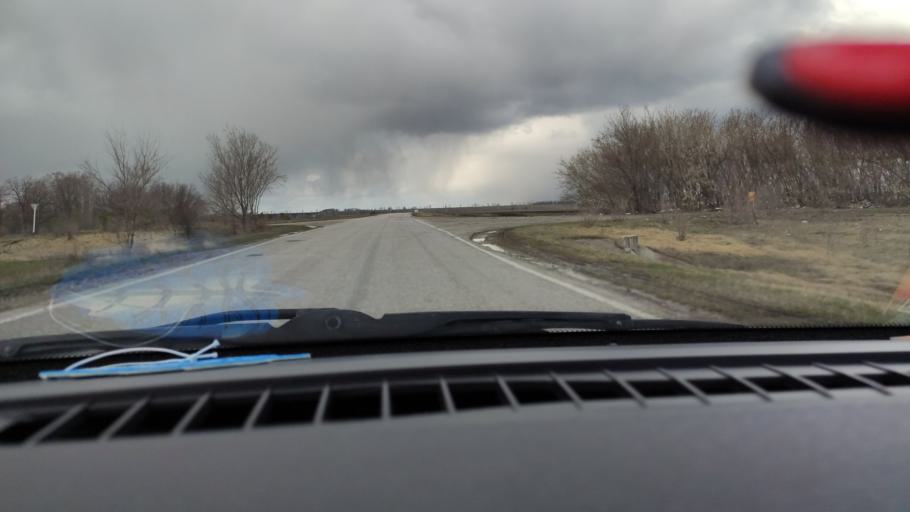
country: RU
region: Samara
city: Povolzhskiy
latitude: 53.7936
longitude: 49.7365
